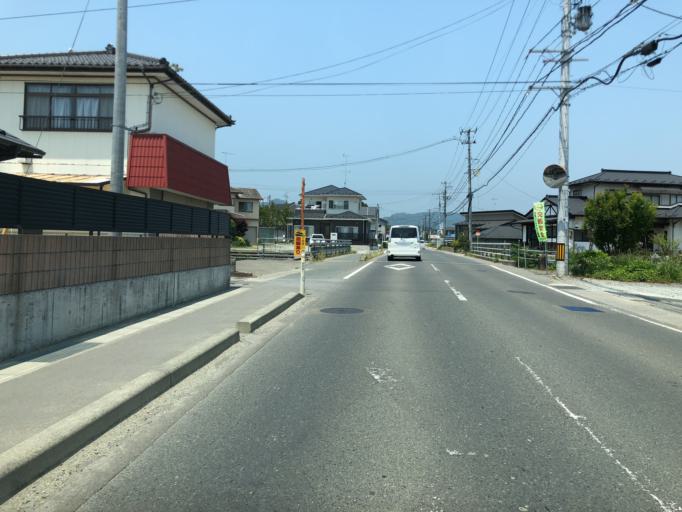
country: JP
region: Miyagi
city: Marumori
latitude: 37.8042
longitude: 140.9085
